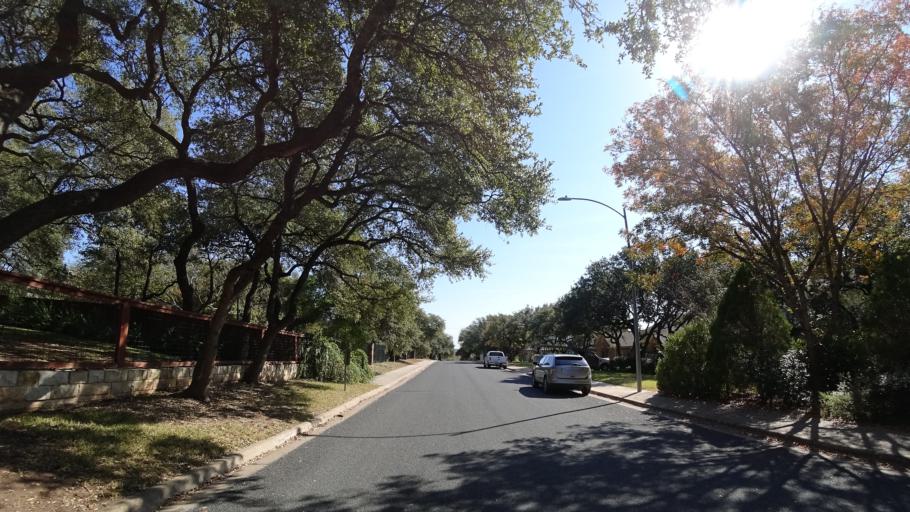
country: US
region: Texas
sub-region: Travis County
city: Barton Creek
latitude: 30.2290
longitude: -97.8729
